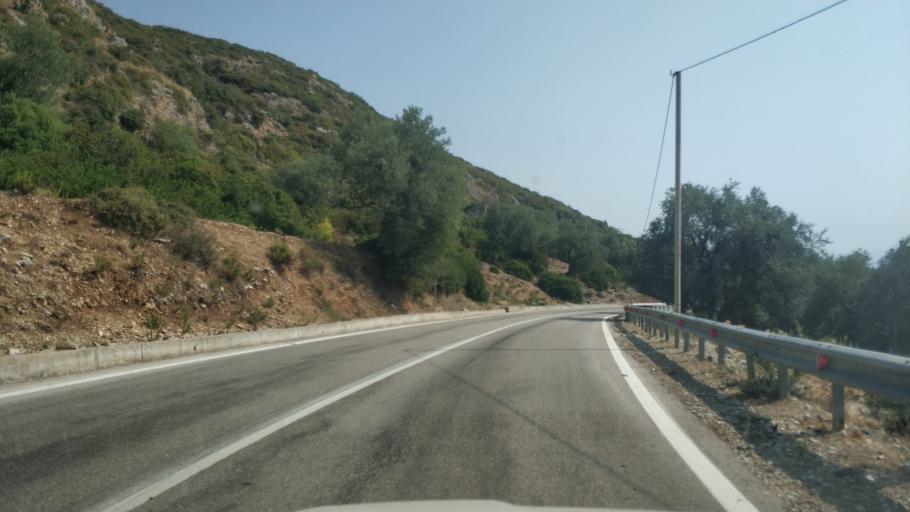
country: AL
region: Vlore
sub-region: Rrethi i Sarandes
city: Lukove
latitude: 40.0247
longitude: 19.8860
